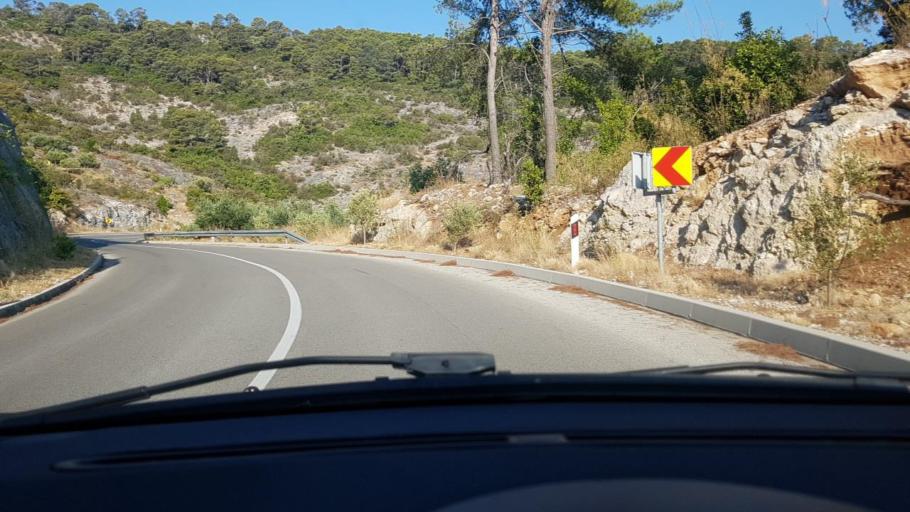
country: HR
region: Dubrovacko-Neretvanska
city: Blato
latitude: 42.7858
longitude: 17.3760
